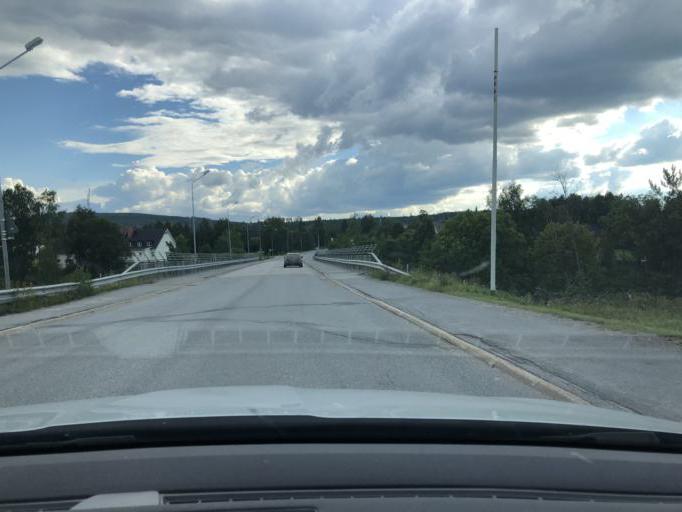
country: SE
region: Vaesternorrland
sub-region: Solleftea Kommun
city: Solleftea
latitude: 63.1810
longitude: 17.0681
